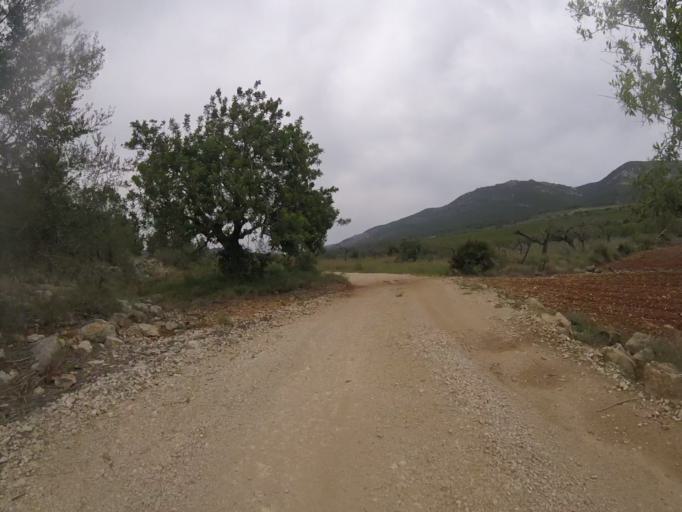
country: ES
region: Valencia
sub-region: Provincia de Castello
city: Alcala de Xivert
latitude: 40.2896
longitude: 0.2597
